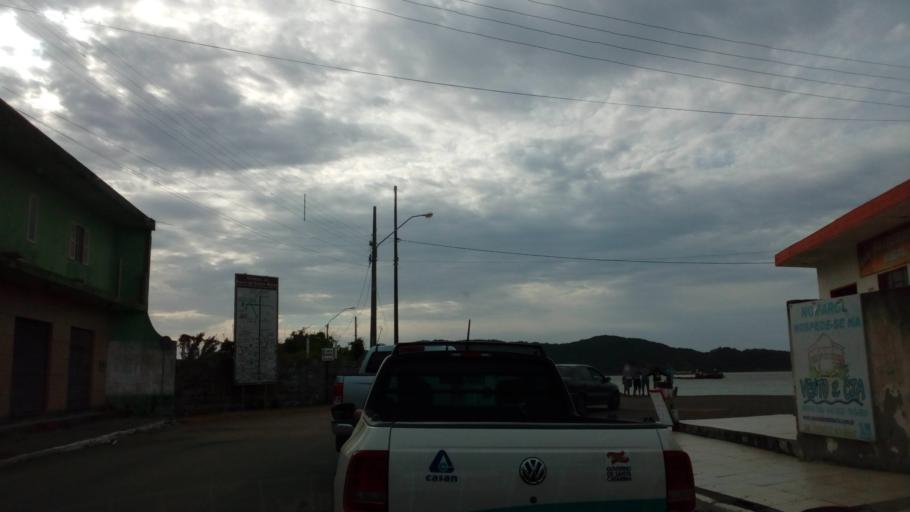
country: BR
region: Santa Catarina
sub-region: Laguna
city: Laguna
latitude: -28.4966
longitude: -48.7752
